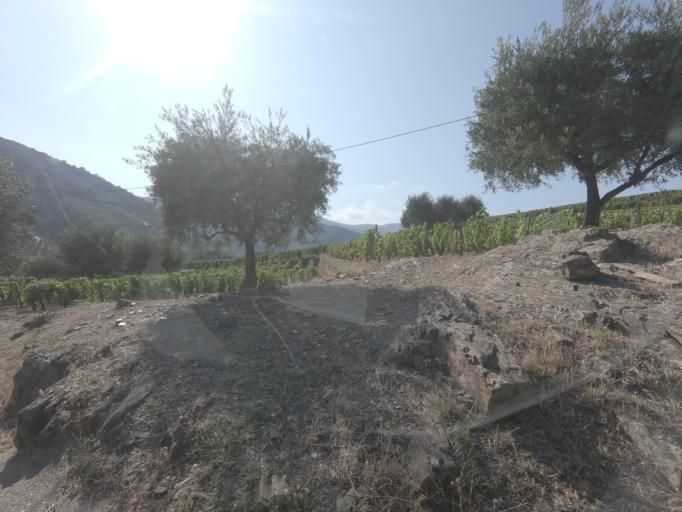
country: PT
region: Viseu
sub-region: Tabuaco
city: Tabuaco
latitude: 41.1852
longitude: -7.5328
